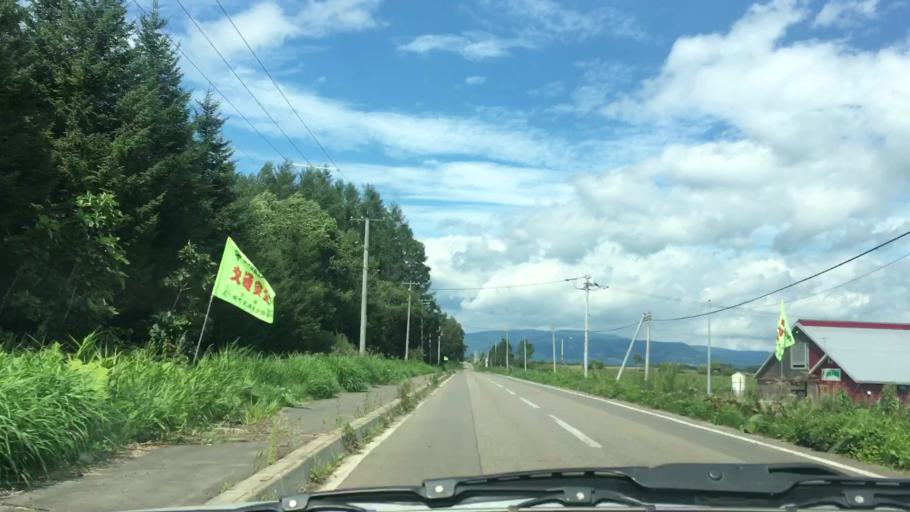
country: JP
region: Hokkaido
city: Otofuke
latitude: 43.2687
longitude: 143.3864
